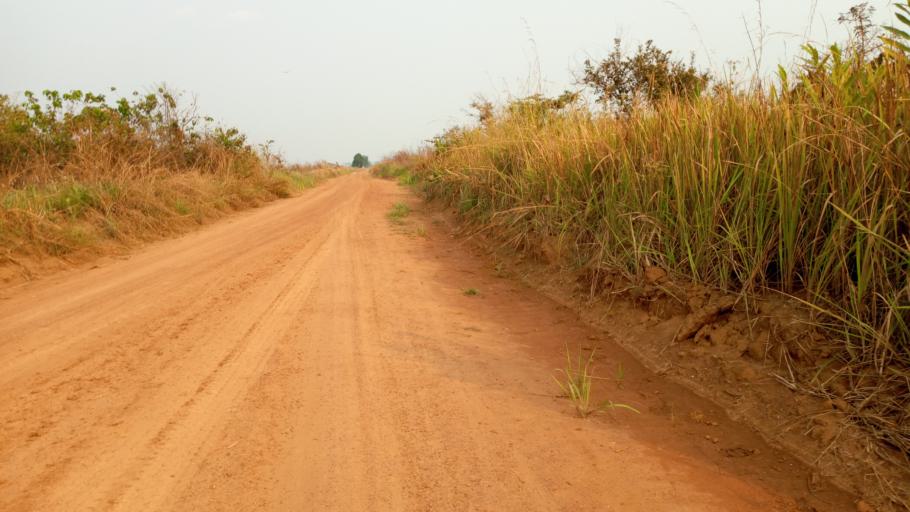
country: CD
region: Bandundu
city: Bandundu
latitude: -3.4084
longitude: 17.5947
